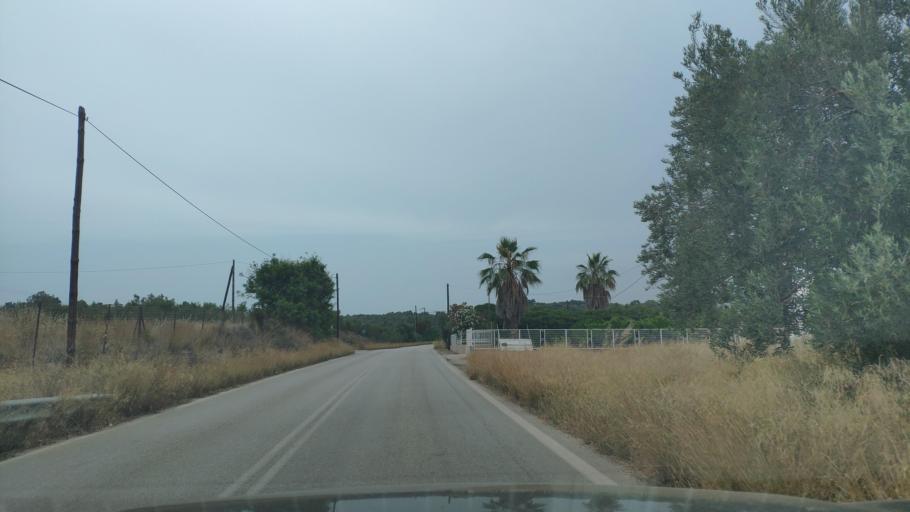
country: GR
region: Peloponnese
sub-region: Nomos Argolidos
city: Porto Cheli
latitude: 37.3159
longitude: 23.1583
